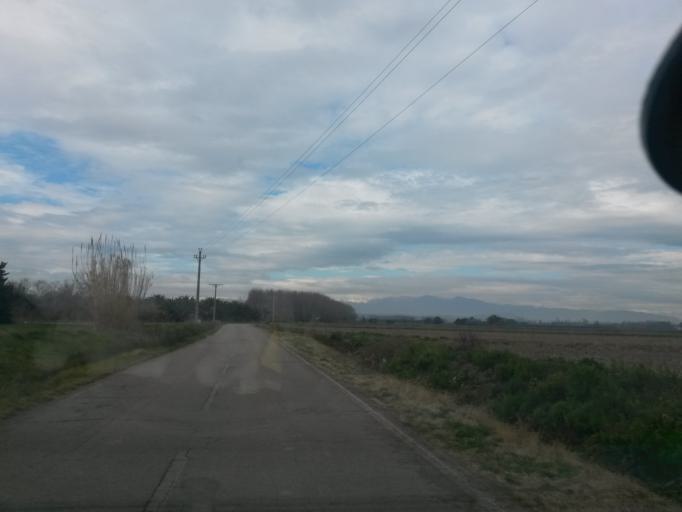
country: ES
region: Catalonia
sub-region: Provincia de Girona
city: Vilabertran
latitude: 42.2846
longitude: 2.9769
